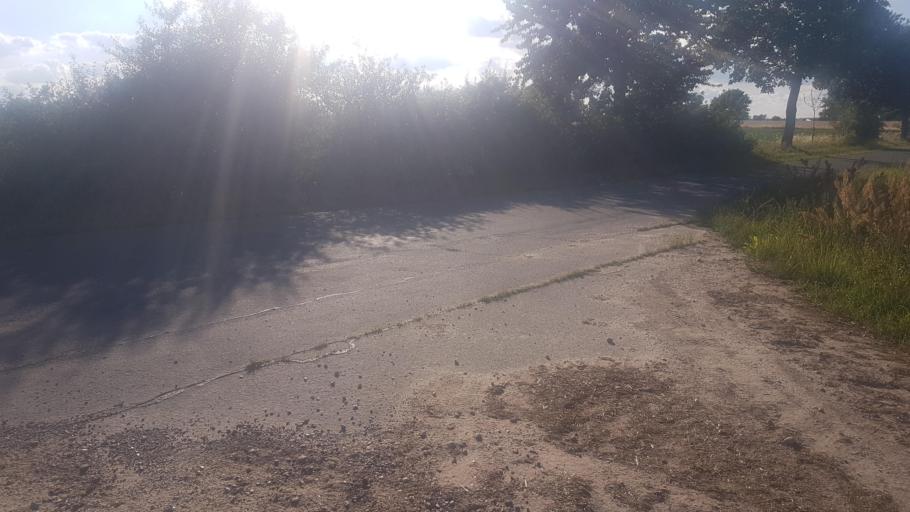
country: DE
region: Lower Saxony
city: Bleckede
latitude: 53.2586
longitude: 10.7711
